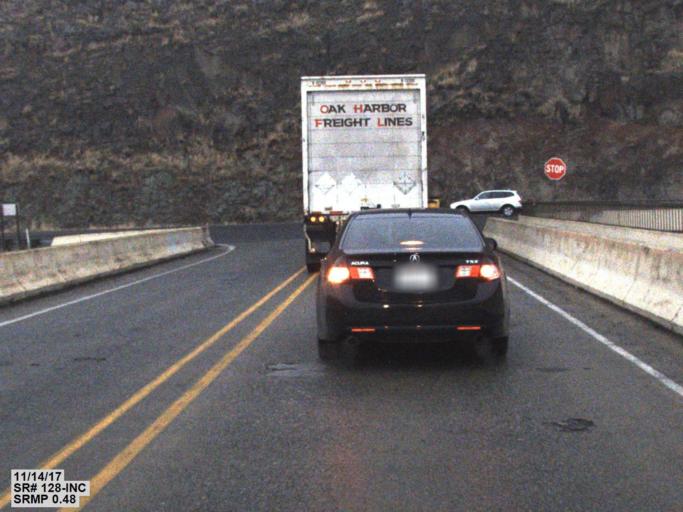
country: US
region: Washington
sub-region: Asotin County
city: West Clarkston-Highland
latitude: 46.4258
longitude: -117.0736
